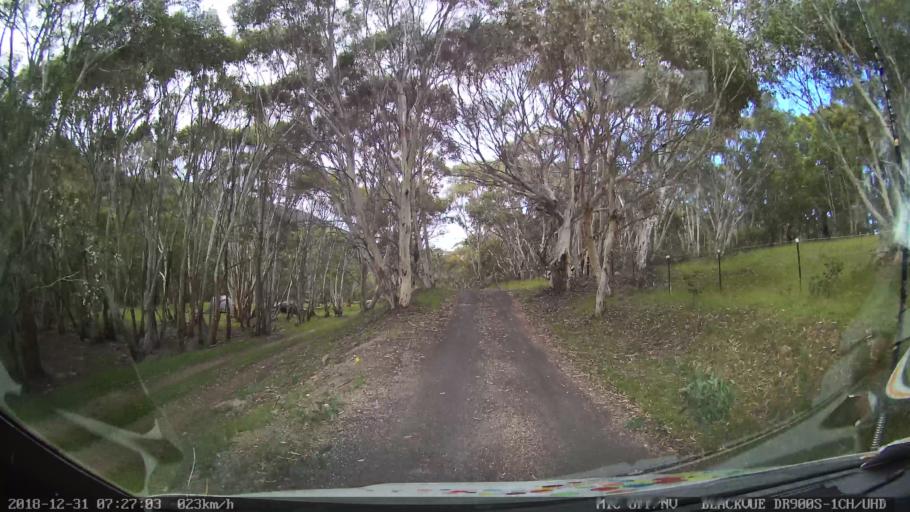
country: AU
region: New South Wales
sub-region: Snowy River
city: Jindabyne
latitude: -36.3203
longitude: 148.4808
